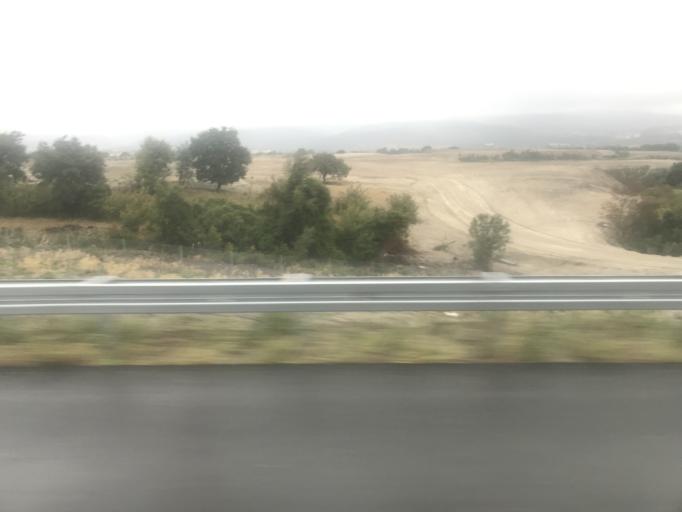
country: TR
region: Balikesir
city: Susurluk
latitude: 39.9462
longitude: 28.1502
